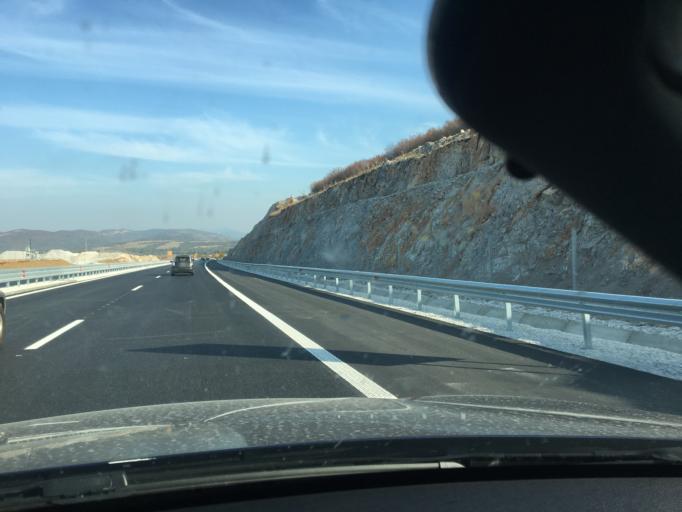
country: BG
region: Lovech
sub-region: Obshtina Yablanitsa
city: Yablanitsa
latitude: 43.0533
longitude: 24.2054
